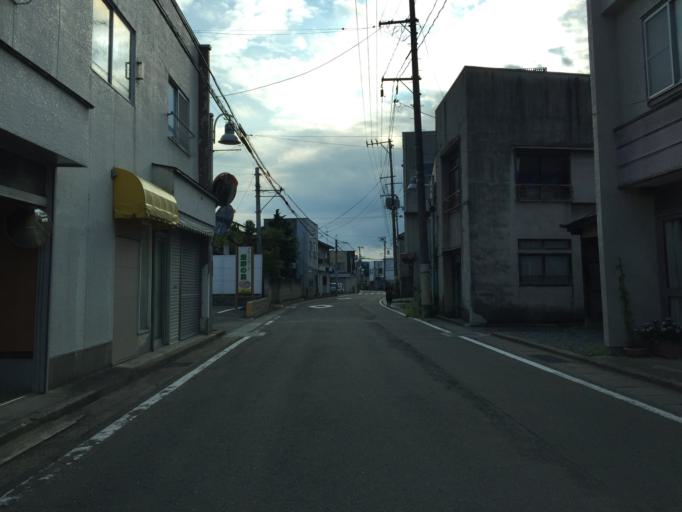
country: JP
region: Fukushima
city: Fukushima-shi
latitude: 37.6565
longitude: 140.5411
